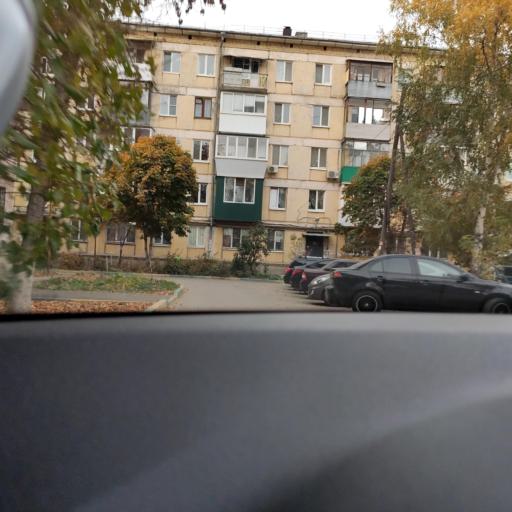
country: RU
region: Samara
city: Samara
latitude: 53.1998
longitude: 50.1851
